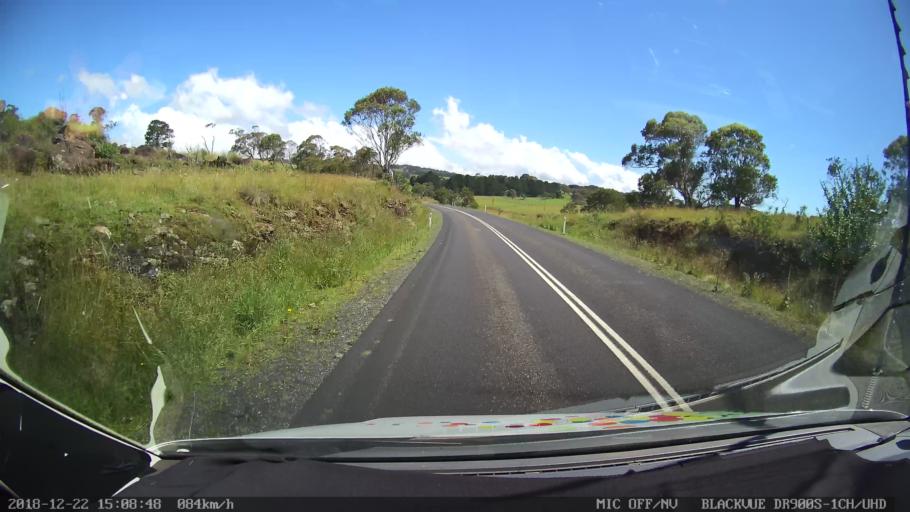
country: AU
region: New South Wales
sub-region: Bellingen
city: Dorrigo
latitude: -30.3170
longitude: 152.4124
